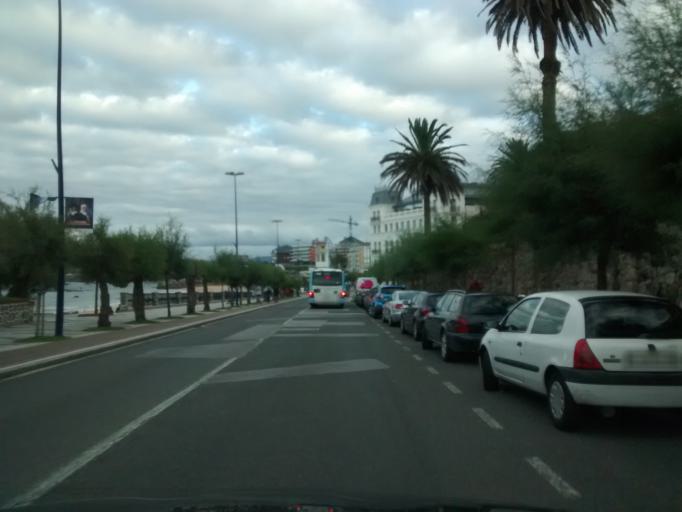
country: ES
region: Cantabria
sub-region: Provincia de Cantabria
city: Santander
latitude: 43.4735
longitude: -3.7843
